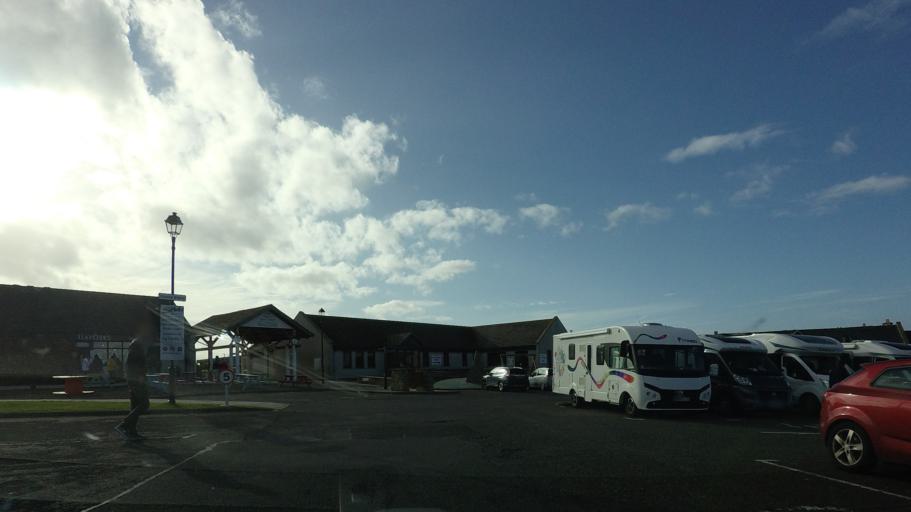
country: GB
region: Scotland
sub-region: Highland
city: Wick
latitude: 58.6429
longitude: -3.0697
